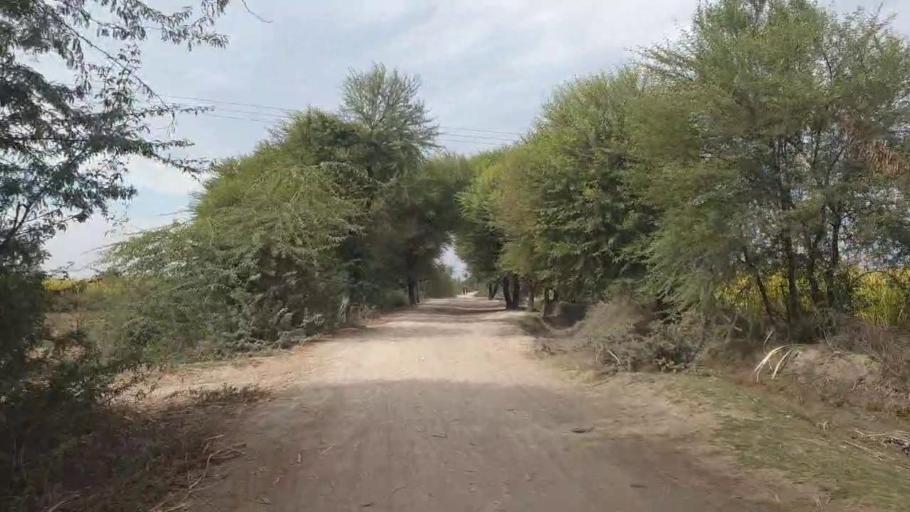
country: PK
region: Sindh
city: Jhol
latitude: 26.0056
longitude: 68.8744
